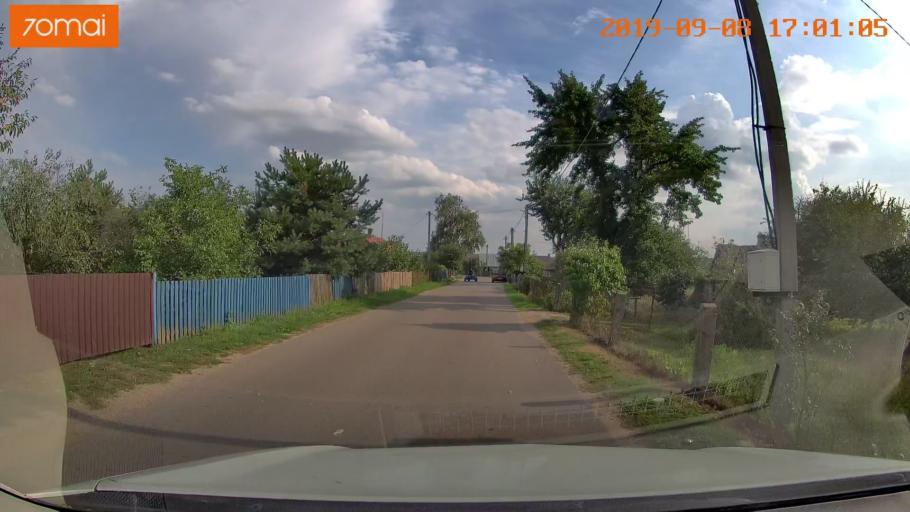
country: BY
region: Grodnenskaya
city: Hrodna
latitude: 53.7120
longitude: 23.9336
